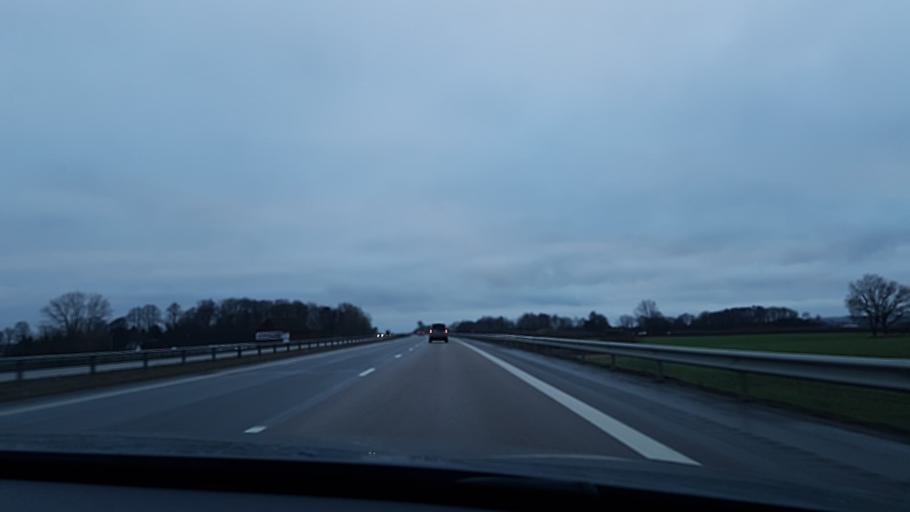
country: SE
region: Skane
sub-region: Astorps Kommun
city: Kvidinge
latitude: 56.1879
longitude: 13.0451
